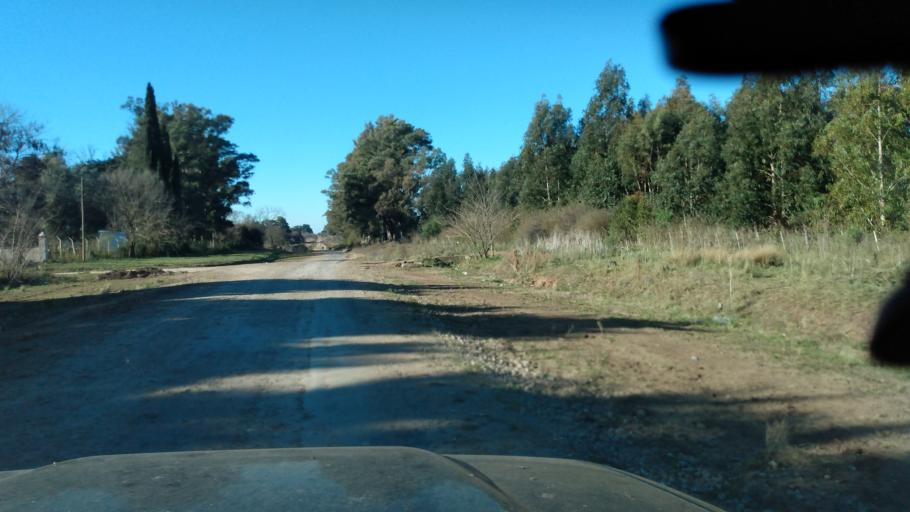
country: AR
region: Buenos Aires
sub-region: Partido de Lujan
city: Lujan
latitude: -34.5672
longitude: -59.1738
